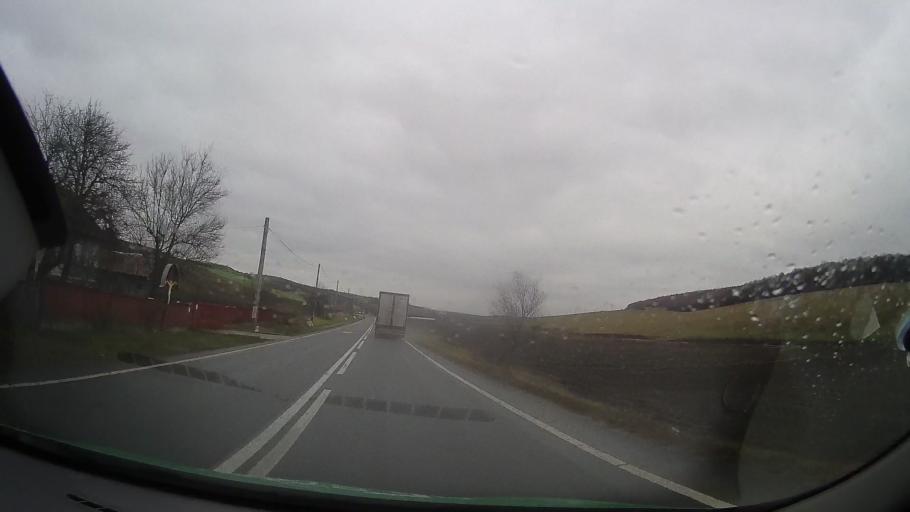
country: RO
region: Mures
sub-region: Comuna Lunca
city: Lunca
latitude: 46.8598
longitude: 24.5573
